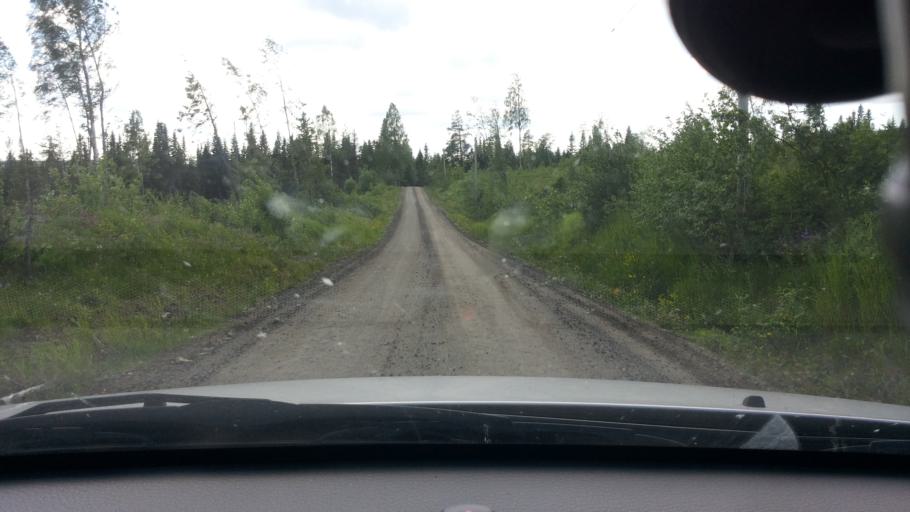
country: SE
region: Vaesternorrland
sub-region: Ange Kommun
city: Fransta
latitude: 62.3477
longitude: 16.3216
